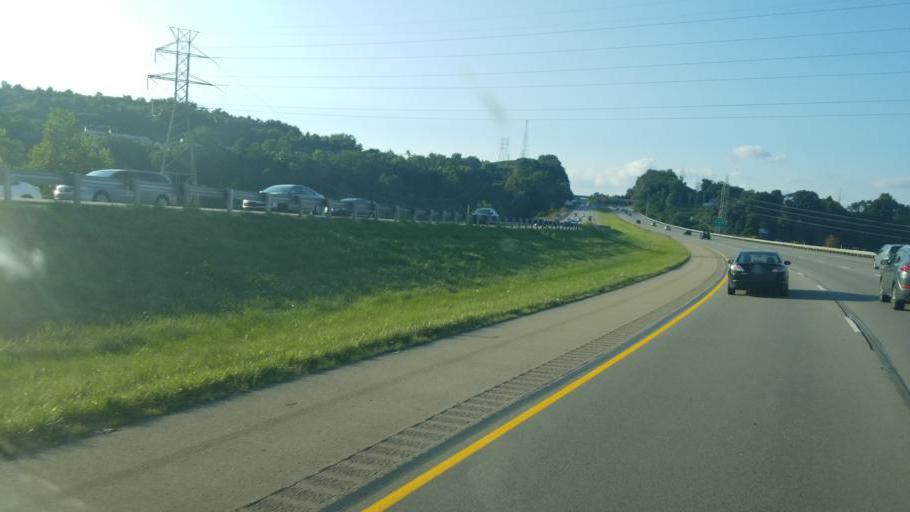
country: US
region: Pennsylvania
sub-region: Allegheny County
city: Heidelberg
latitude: 40.3830
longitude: -80.0963
